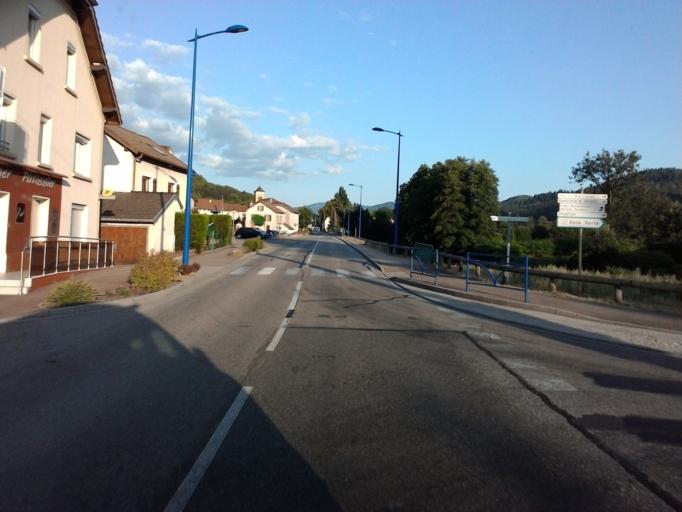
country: FR
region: Lorraine
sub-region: Departement des Vosges
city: Ramonchamp
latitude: 47.9086
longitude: 6.7058
